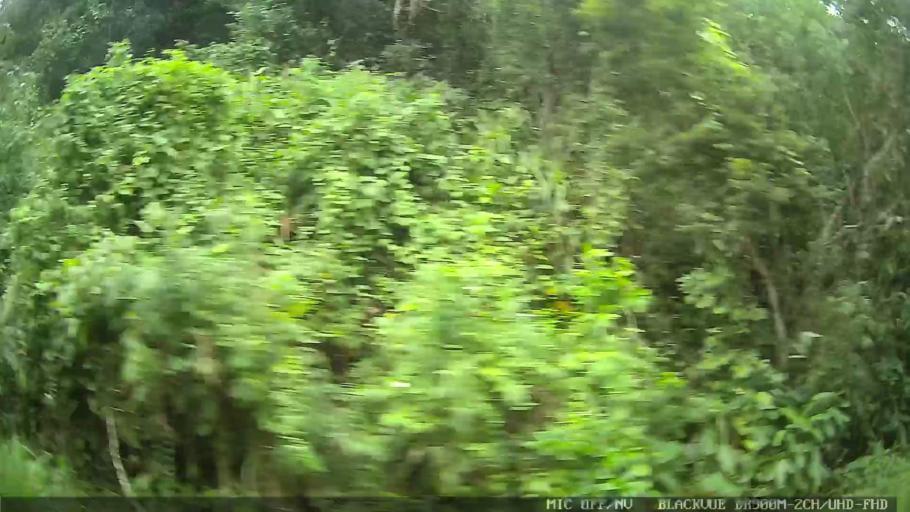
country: BR
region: Sao Paulo
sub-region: Iguape
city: Iguape
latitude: -24.7000
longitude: -47.5369
